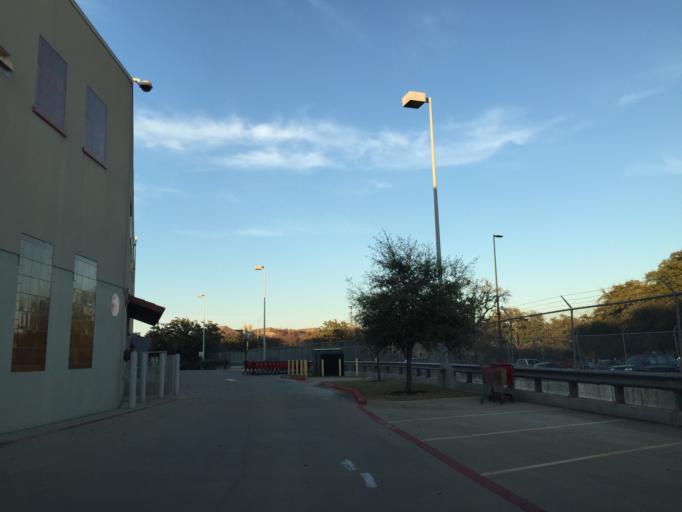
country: US
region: Texas
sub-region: Williamson County
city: Jollyville
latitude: 30.3922
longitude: -97.7437
